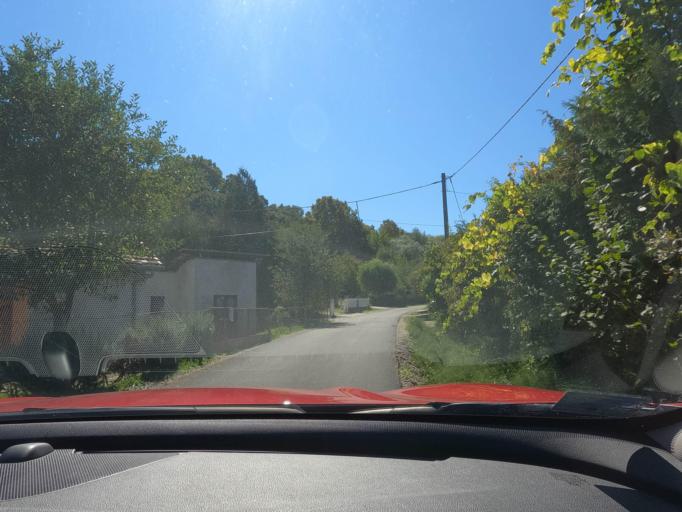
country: HR
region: Sisacko-Moslavacka
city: Petrinja
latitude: 45.4293
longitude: 16.2676
